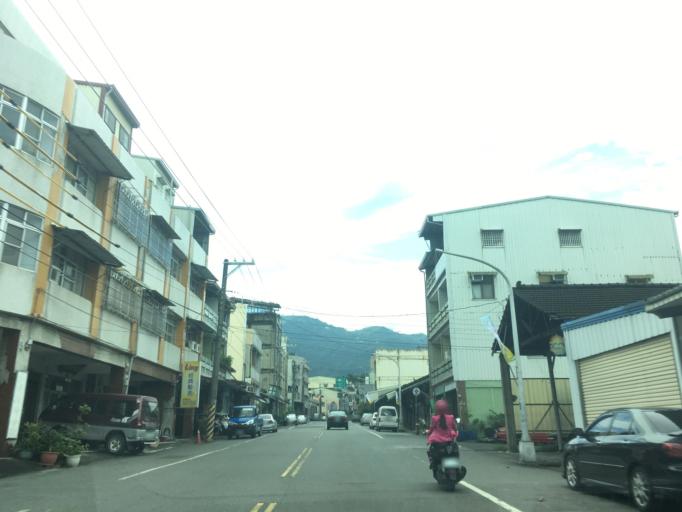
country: TW
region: Taiwan
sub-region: Yunlin
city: Douliu
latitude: 23.5843
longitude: 120.5588
